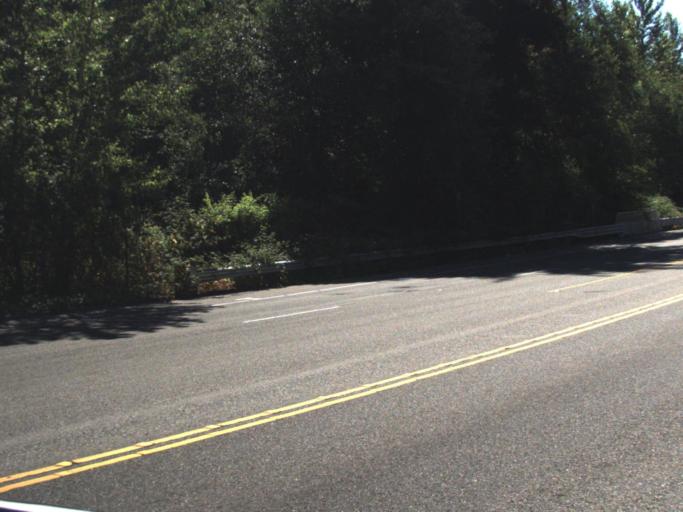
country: US
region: Washington
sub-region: King County
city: Issaquah
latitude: 47.5405
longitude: -122.0633
